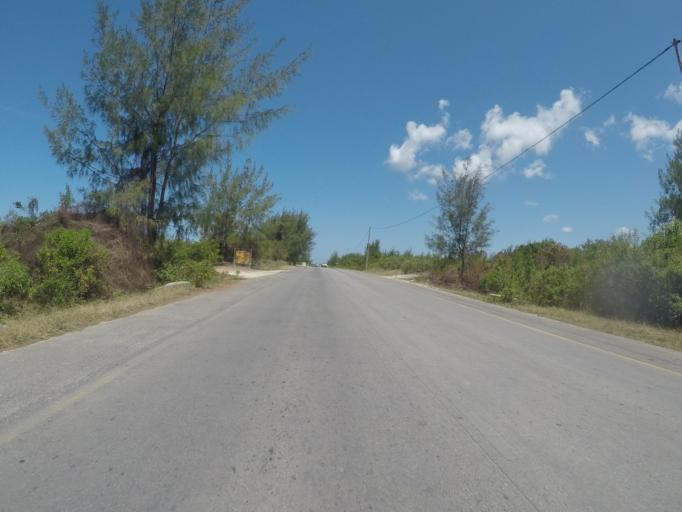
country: TZ
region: Zanzibar Central/South
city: Nganane
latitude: -6.2849
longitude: 39.5361
